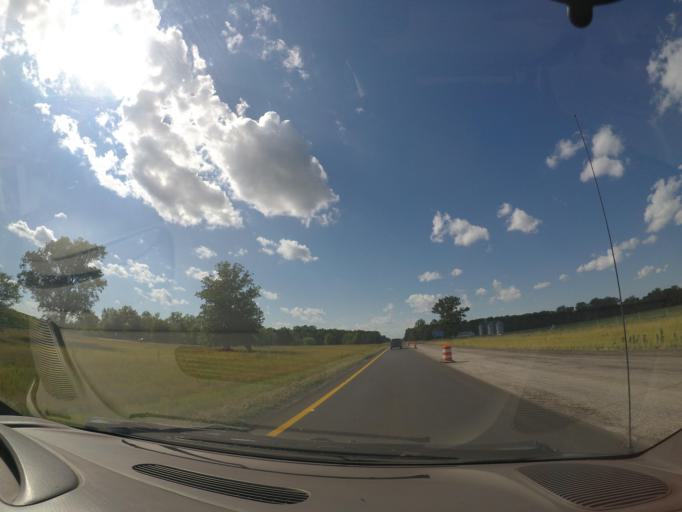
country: US
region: Ohio
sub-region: Sandusky County
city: Fremont
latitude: 41.3348
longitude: -83.0607
